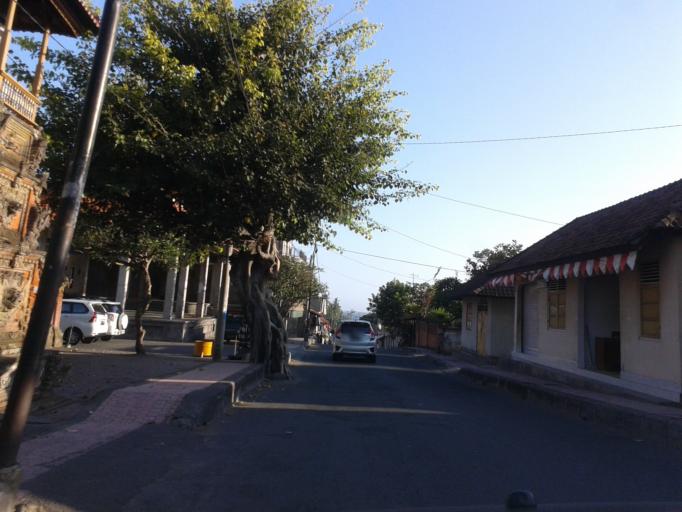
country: ID
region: Bali
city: Semarapura
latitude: -8.5651
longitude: 115.3850
